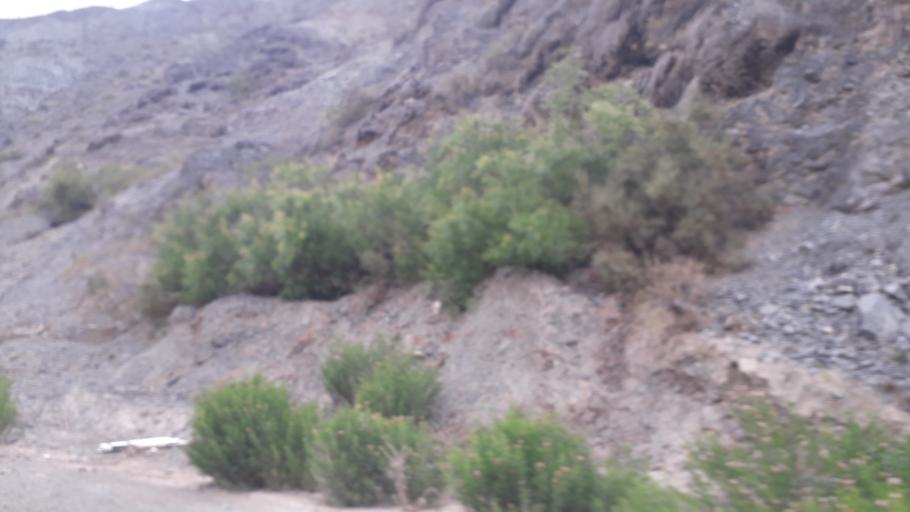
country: AR
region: Jujuy
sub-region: Departamento de Tumbaya
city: Tumbaya
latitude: -23.8096
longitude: -65.4778
